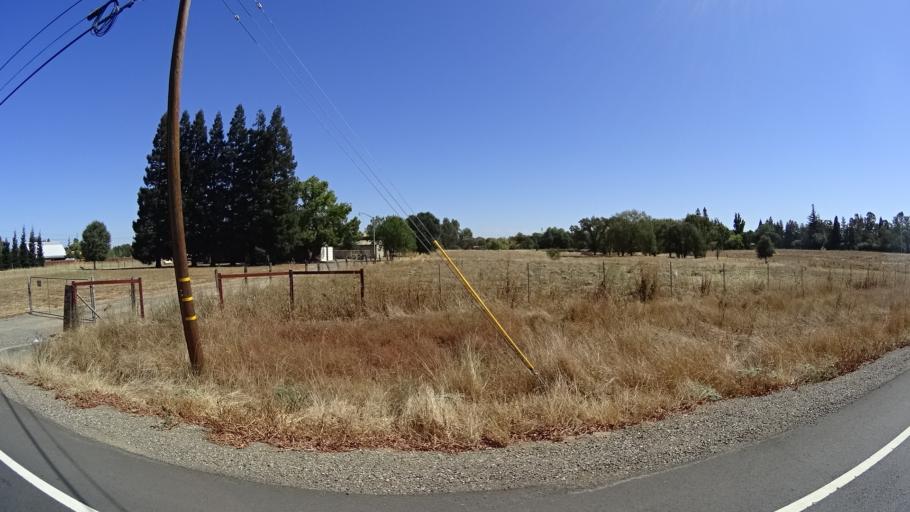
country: US
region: California
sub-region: Sacramento County
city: Vineyard
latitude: 38.4399
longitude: -121.3347
